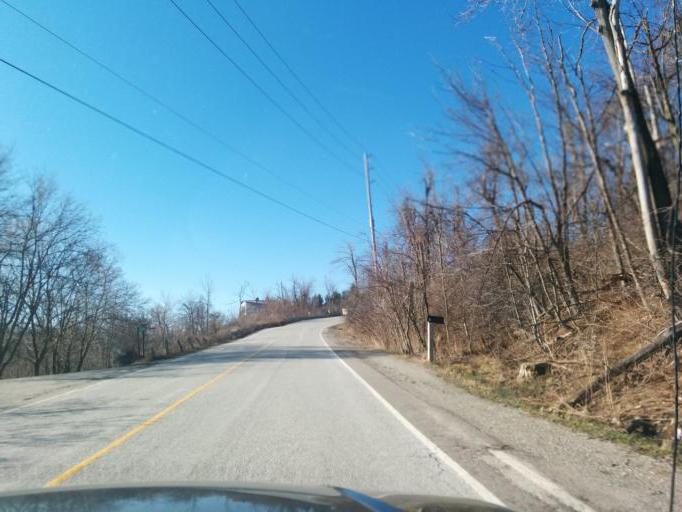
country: CA
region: Ontario
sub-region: Halton
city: Milton
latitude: 43.5010
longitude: -79.9149
